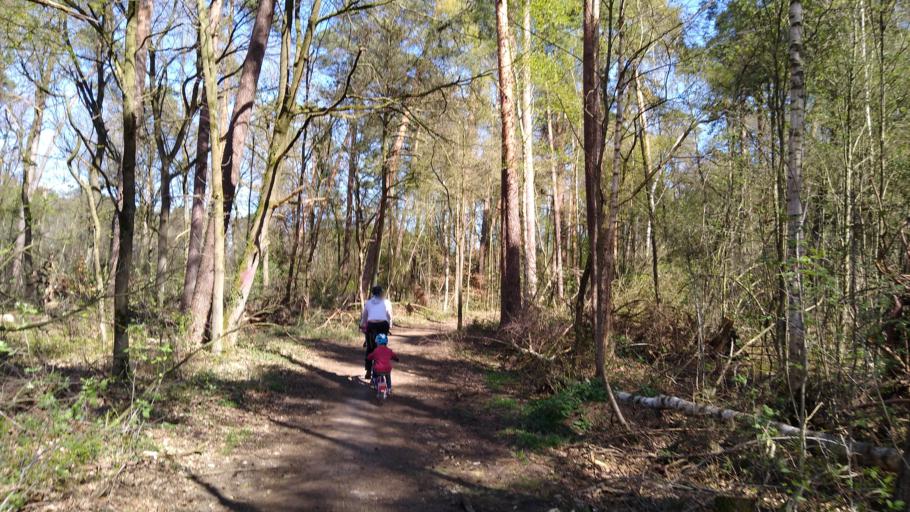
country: DE
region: North Rhine-Westphalia
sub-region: Regierungsbezirk Detmold
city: Verl
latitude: 51.8943
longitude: 8.5611
